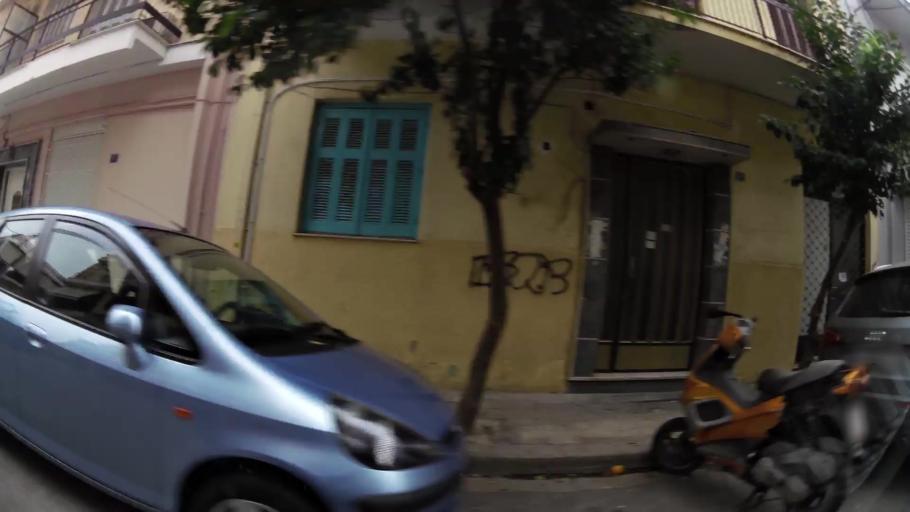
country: GR
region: Attica
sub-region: Nomos Piraios
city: Agios Ioannis Rentis
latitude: 37.9556
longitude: 23.6616
